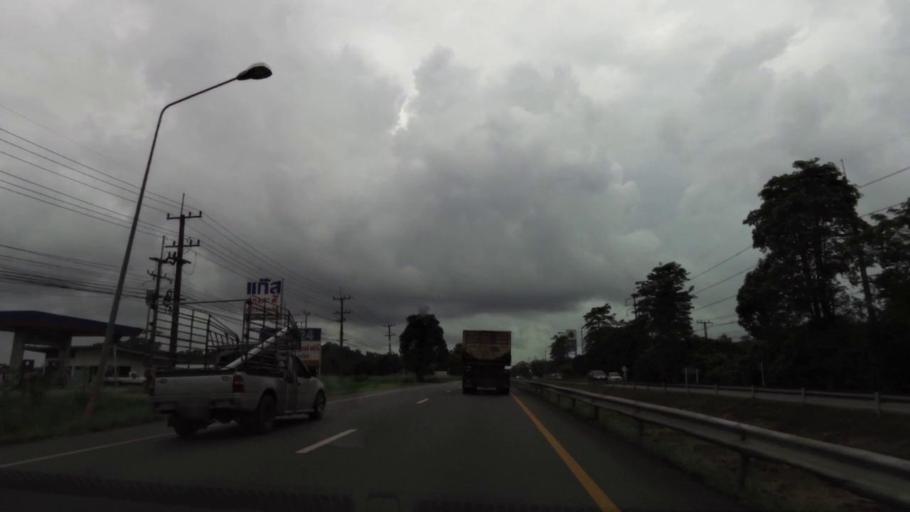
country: TH
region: Chanthaburi
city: Chanthaburi
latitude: 12.6595
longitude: 102.0644
